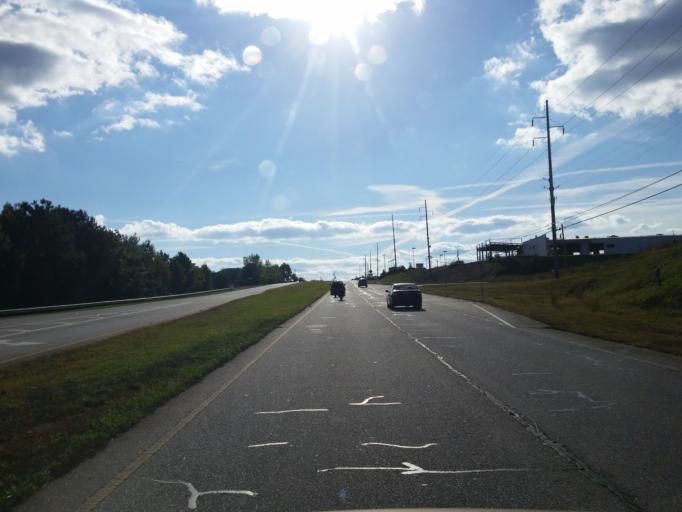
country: US
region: Georgia
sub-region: Paulding County
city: Hiram
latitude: 33.9199
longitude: -84.7633
